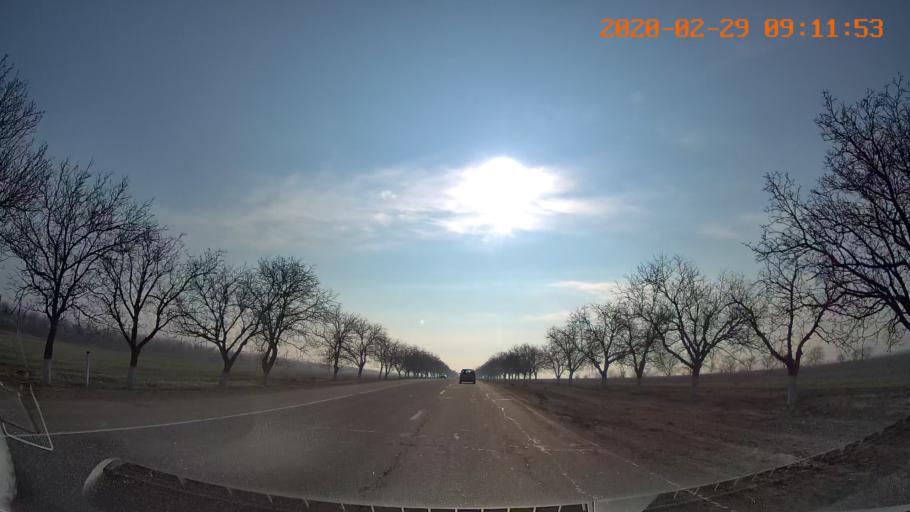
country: MD
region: Telenesti
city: Slobozia
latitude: 46.8312
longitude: 29.8076
